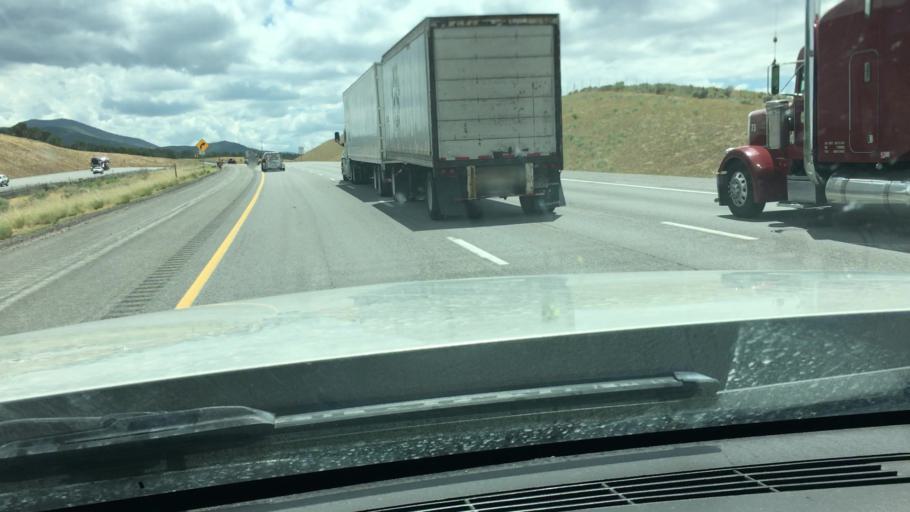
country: US
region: Utah
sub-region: Beaver County
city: Beaver
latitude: 38.4804
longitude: -112.6162
